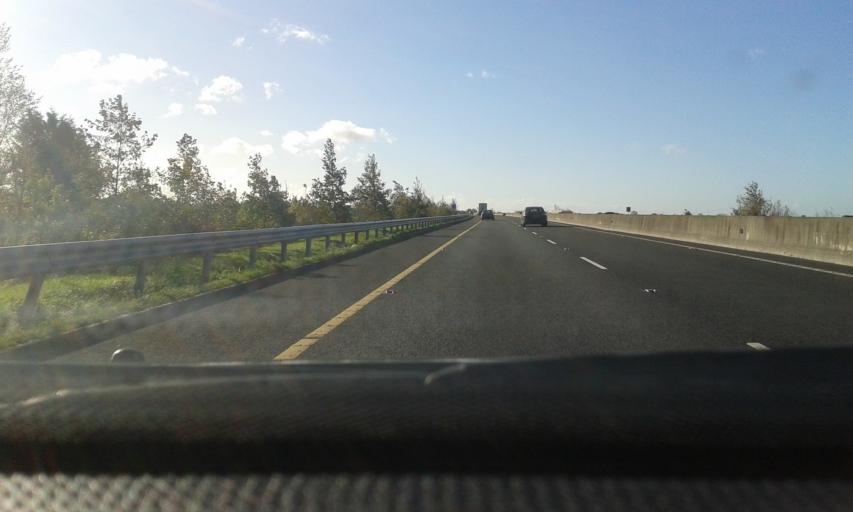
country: IE
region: Leinster
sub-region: Laois
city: Rathdowney
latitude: 52.7792
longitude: -7.5353
